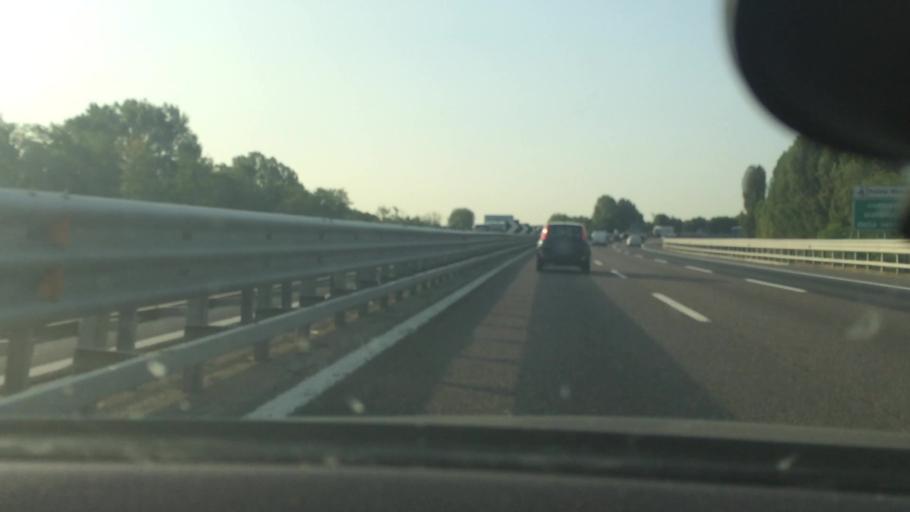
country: IT
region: Lombardy
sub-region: Citta metropolitana di Milano
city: Figino
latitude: 45.4761
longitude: 9.0785
